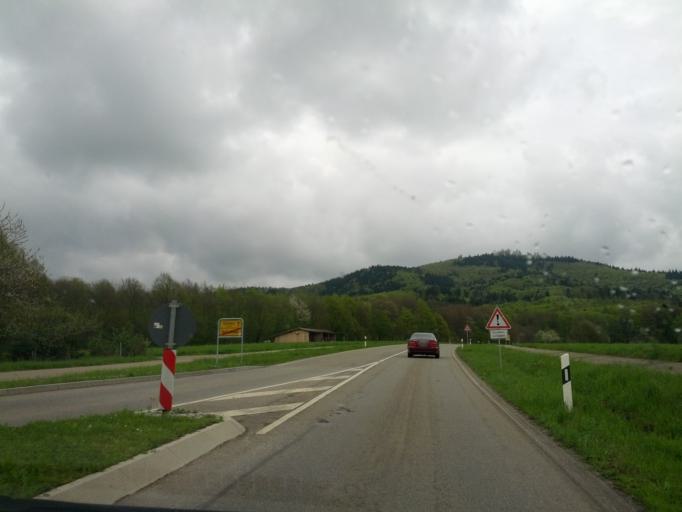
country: DE
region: Baden-Wuerttemberg
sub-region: Freiburg Region
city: Bollschweil
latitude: 47.9239
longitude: 7.7965
